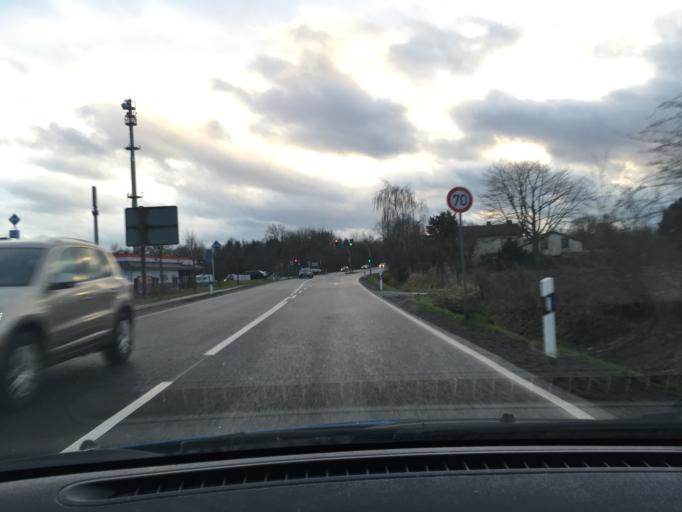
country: DE
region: Schleswig-Holstein
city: Ellerhoop
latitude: 53.7200
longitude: 9.7596
